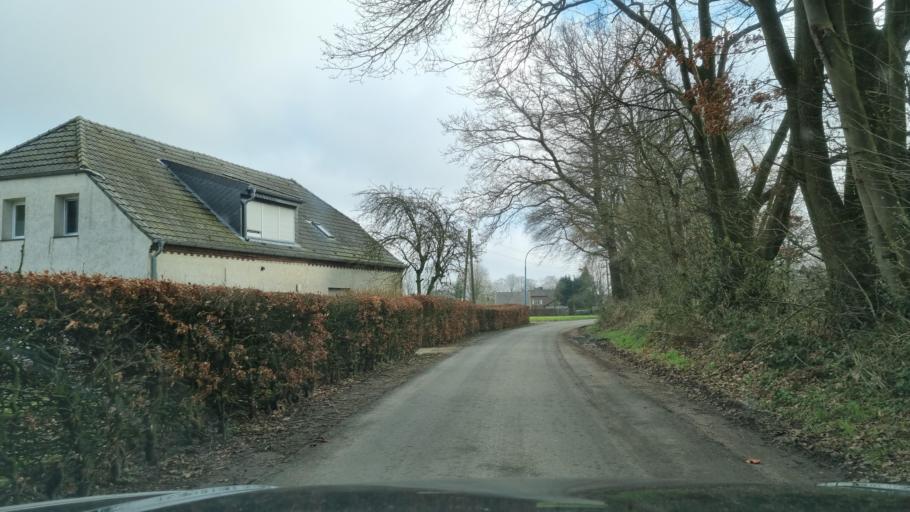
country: DE
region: North Rhine-Westphalia
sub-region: Regierungsbezirk Dusseldorf
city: Kleve
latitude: 51.7509
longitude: 6.1552
